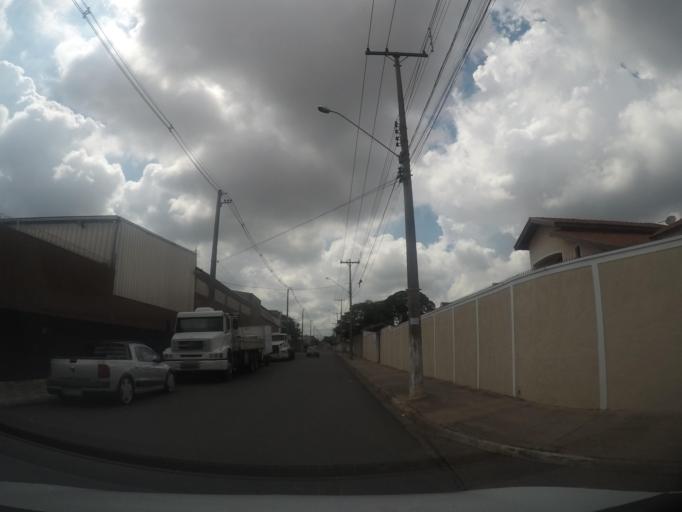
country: BR
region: Sao Paulo
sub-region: Hortolandia
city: Hortolandia
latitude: -22.8526
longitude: -47.1642
